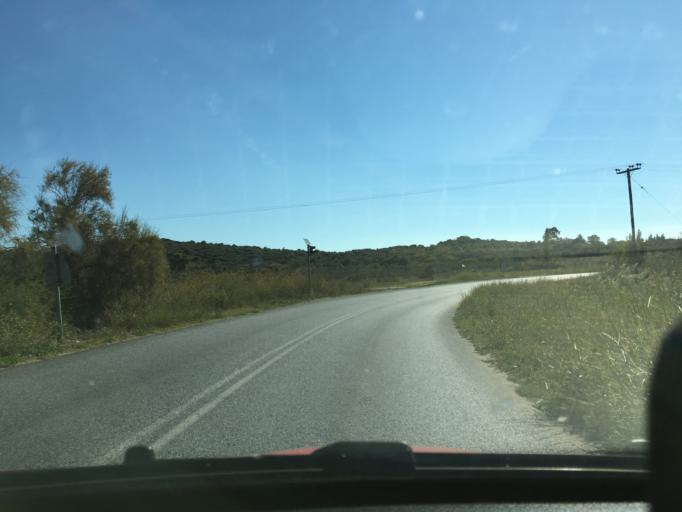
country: GR
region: Central Macedonia
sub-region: Nomos Chalkidikis
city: Nea Roda
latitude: 40.3780
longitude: 23.9255
